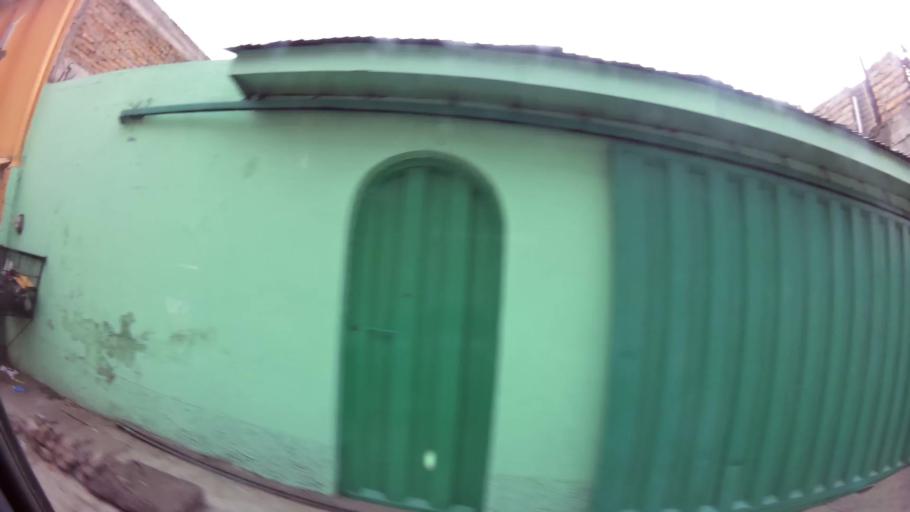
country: HN
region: Francisco Morazan
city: Tegucigalpa
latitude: 14.0985
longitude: -87.1706
